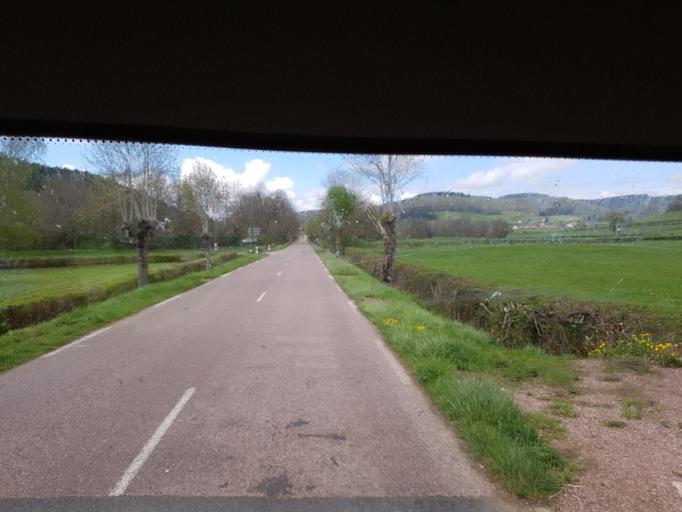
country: FR
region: Bourgogne
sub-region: Departement de Saone-et-Loire
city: Autun
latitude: 47.0718
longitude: 4.2485
